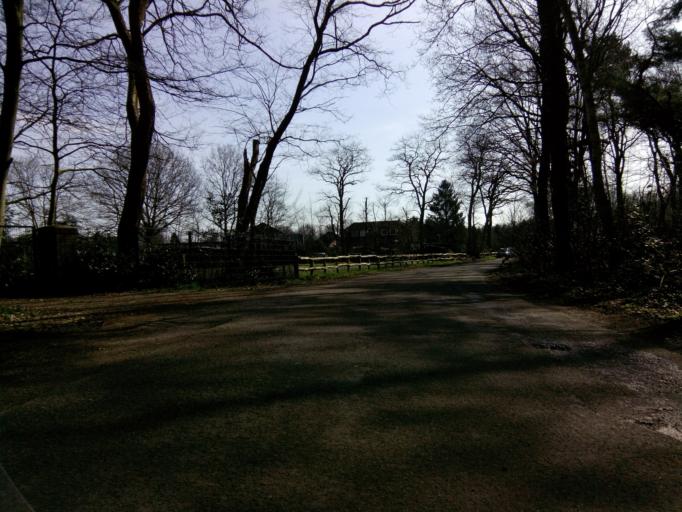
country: NL
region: Gelderland
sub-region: Gemeente Barneveld
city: Voorthuizen
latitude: 52.2145
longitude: 5.6149
